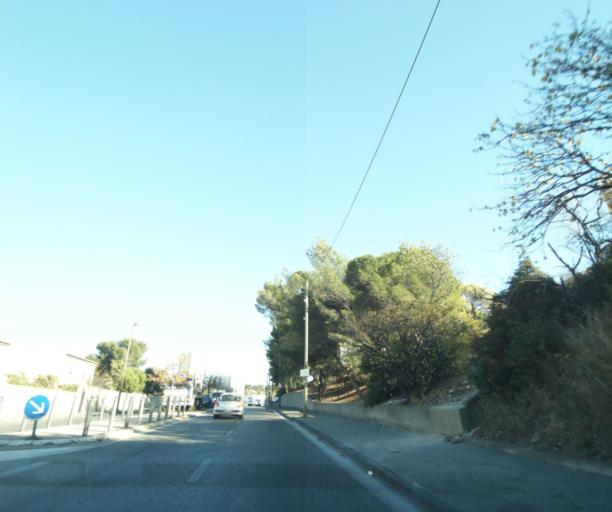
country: FR
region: Provence-Alpes-Cote d'Azur
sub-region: Departement des Bouches-du-Rhone
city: Marseille 14
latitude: 43.3488
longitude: 5.3725
